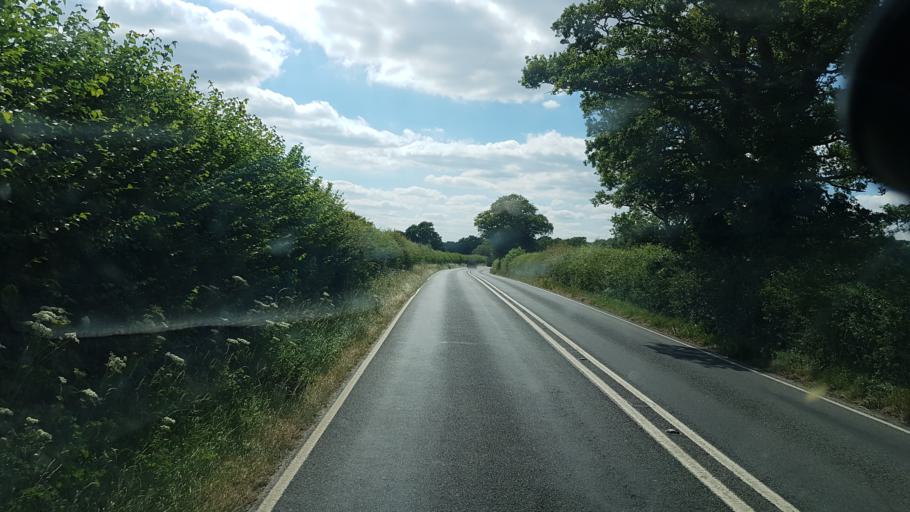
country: GB
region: England
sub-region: West Sussex
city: Southwater
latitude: 50.9932
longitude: -0.3542
